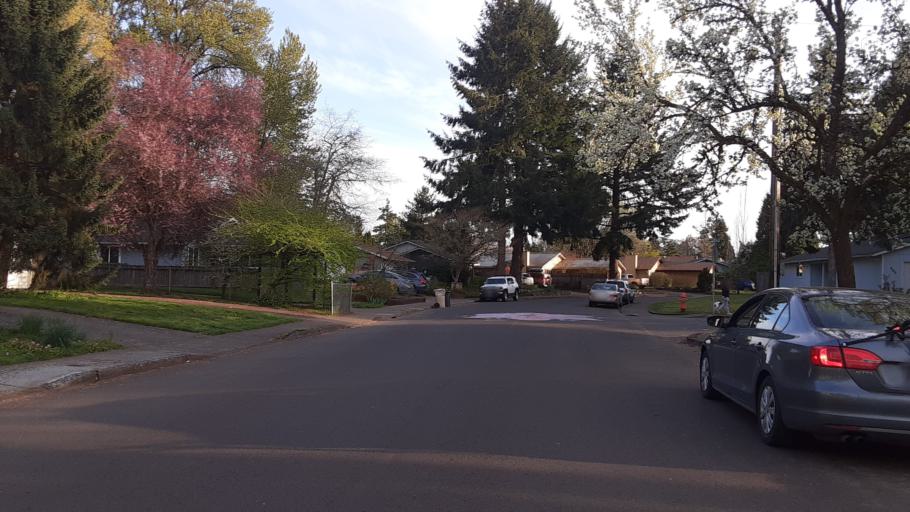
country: US
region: Oregon
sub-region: Benton County
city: Corvallis
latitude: 44.5483
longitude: -123.2587
